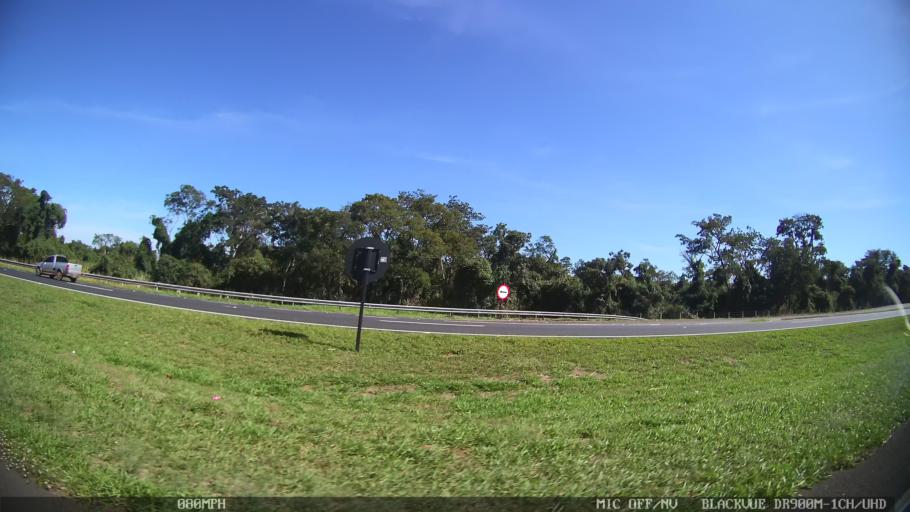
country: BR
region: Sao Paulo
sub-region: Santa Rita Do Passa Quatro
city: Santa Rita do Passa Quatro
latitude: -21.6307
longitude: -47.6135
